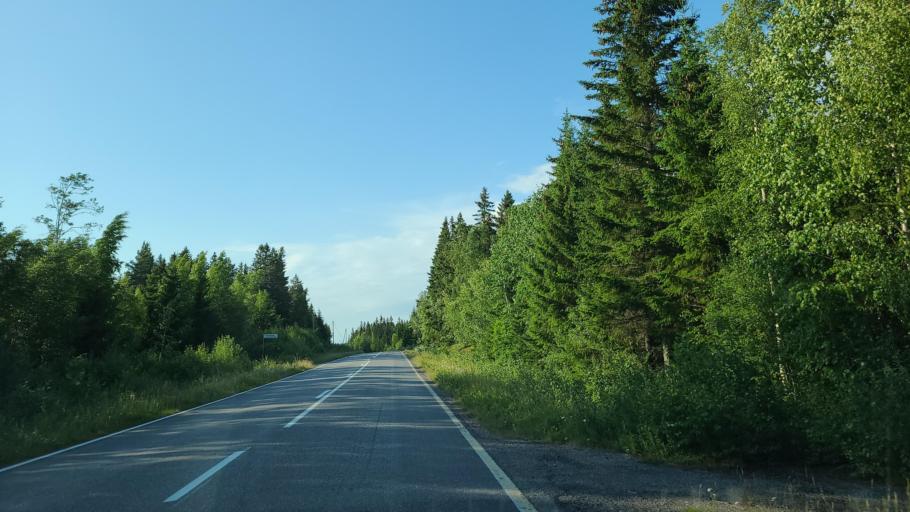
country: FI
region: Ostrobothnia
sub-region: Vaasa
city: Replot
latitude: 63.3115
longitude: 21.3603
